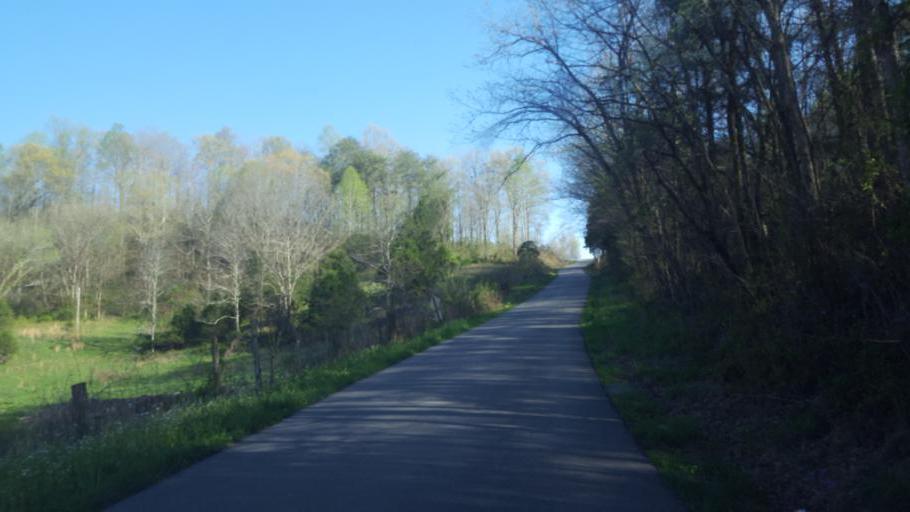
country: US
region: Kentucky
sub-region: Barren County
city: Cave City
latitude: 37.1759
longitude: -86.0021
